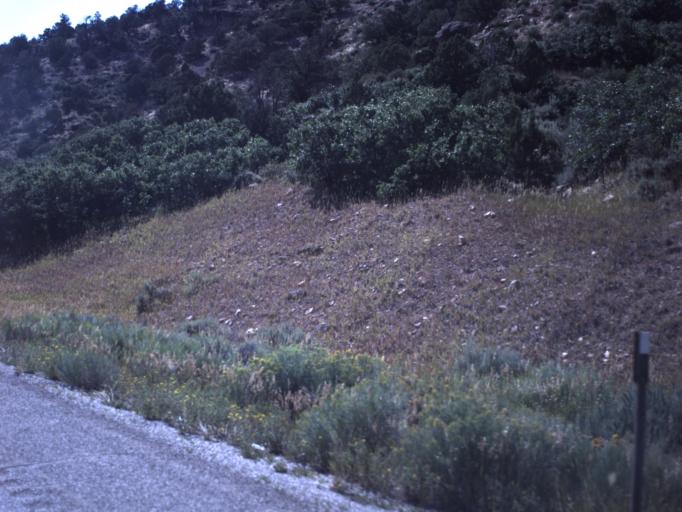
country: US
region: Utah
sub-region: Carbon County
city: Helper
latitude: 40.1956
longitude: -110.9315
